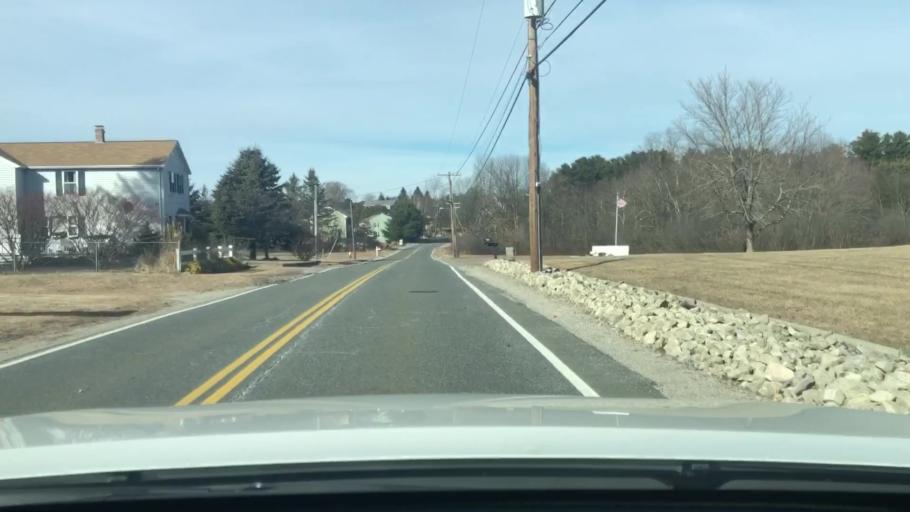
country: US
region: Massachusetts
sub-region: Worcester County
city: Blackstone
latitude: 42.0529
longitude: -71.5221
